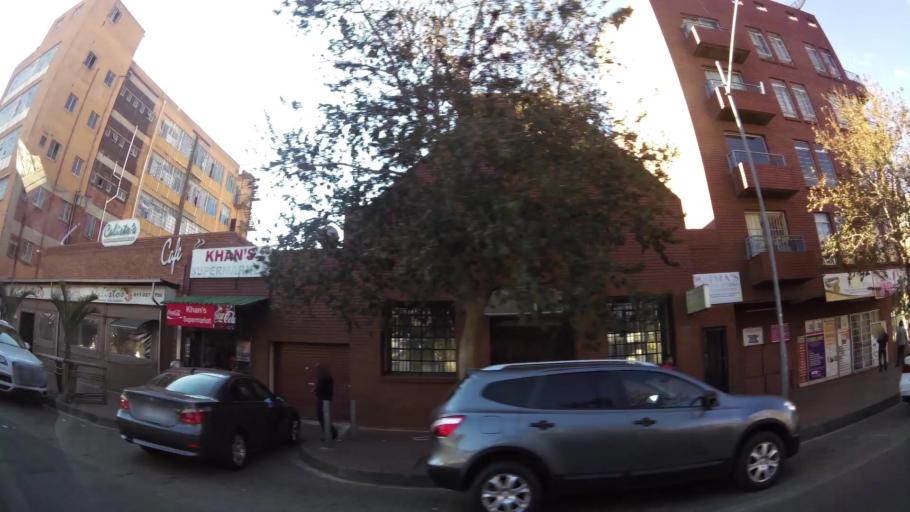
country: ZA
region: Gauteng
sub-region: City of Johannesburg Metropolitan Municipality
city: Johannesburg
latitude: -26.2038
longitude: 28.0222
